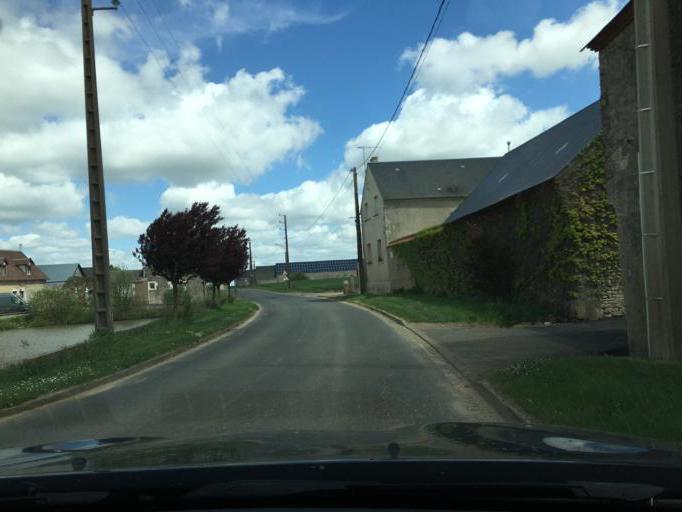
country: FR
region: Centre
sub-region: Departement du Loiret
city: Bricy
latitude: 48.0351
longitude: 1.8018
